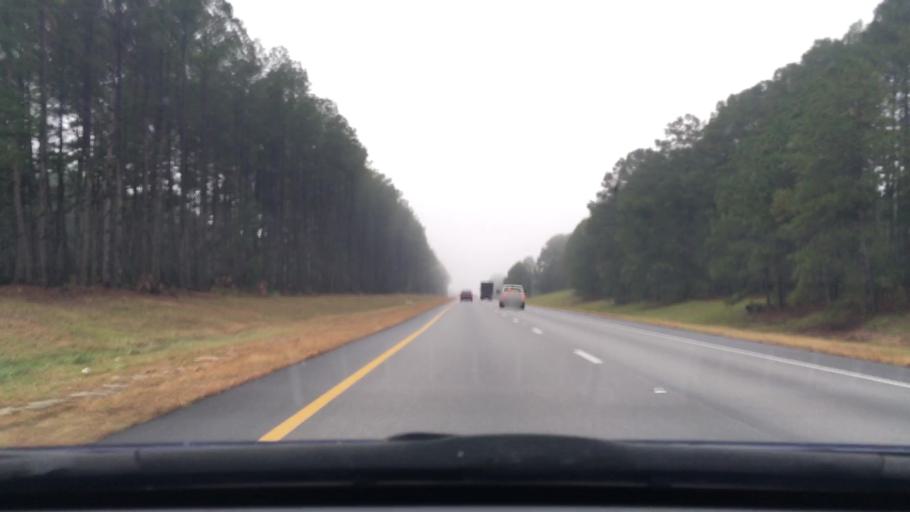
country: US
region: South Carolina
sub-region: Lee County
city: Bishopville
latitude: 34.2038
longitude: -80.3732
